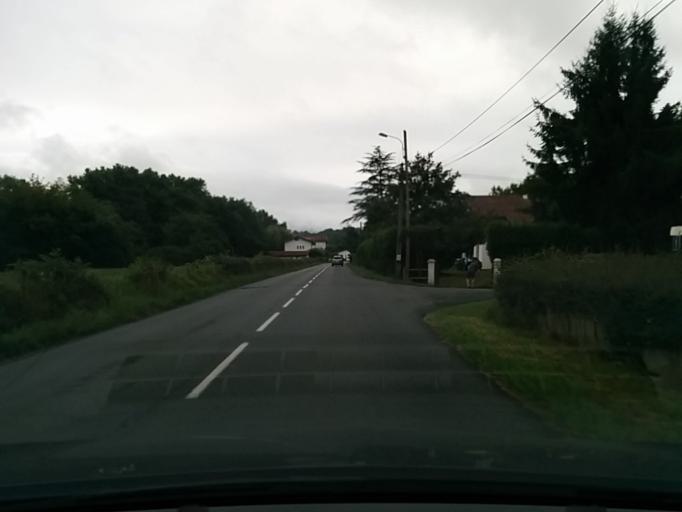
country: FR
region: Aquitaine
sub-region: Departement des Pyrenees-Atlantiques
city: Saint-Pee-sur-Nivelle
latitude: 43.3241
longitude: -1.5492
